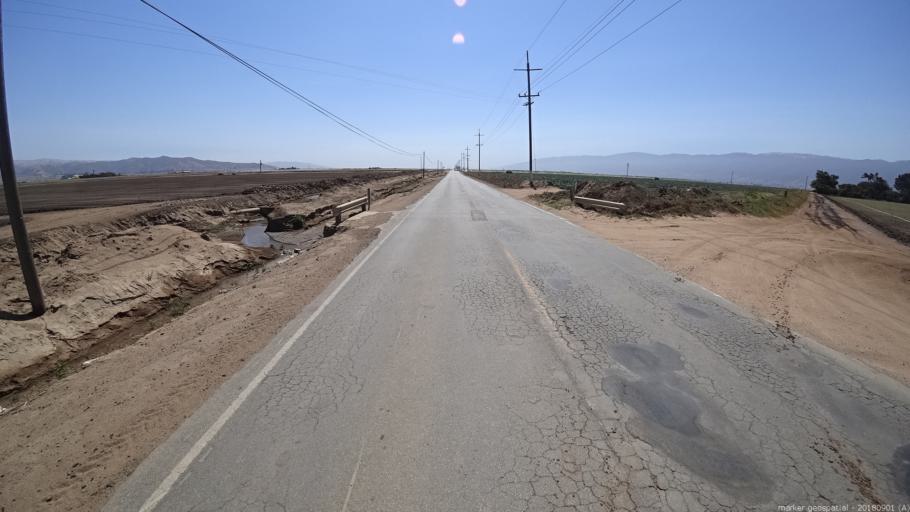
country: US
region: California
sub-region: Monterey County
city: Chualar
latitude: 36.6019
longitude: -121.5114
